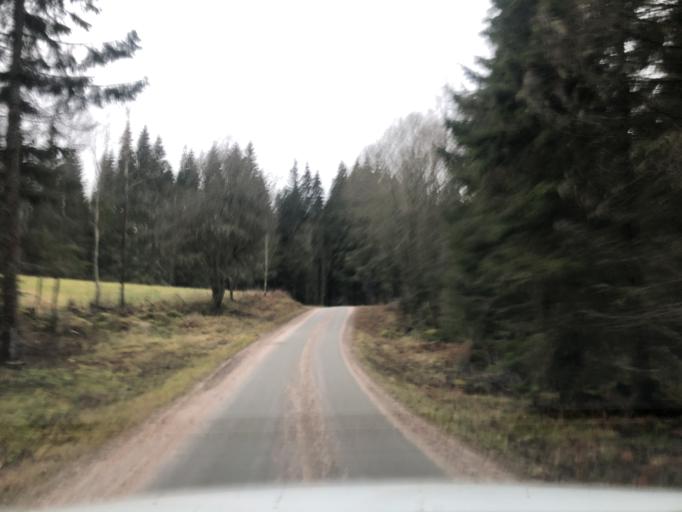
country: SE
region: Vaestra Goetaland
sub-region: Ulricehamns Kommun
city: Ulricehamn
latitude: 57.8737
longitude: 13.5606
